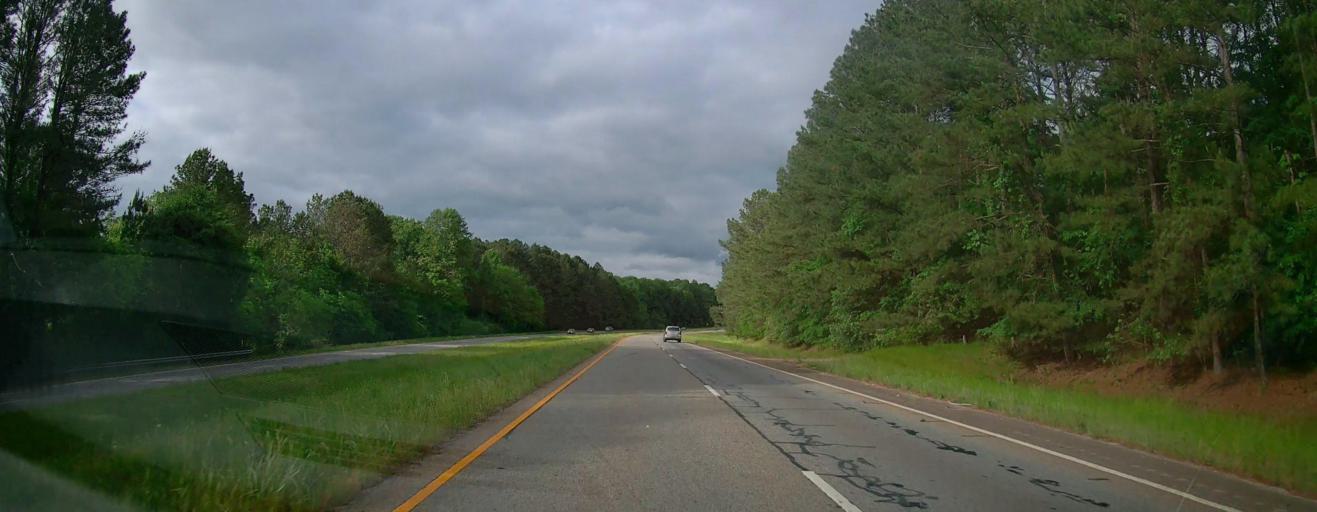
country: US
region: Georgia
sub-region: Barrow County
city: Statham
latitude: 33.8856
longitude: -83.5887
